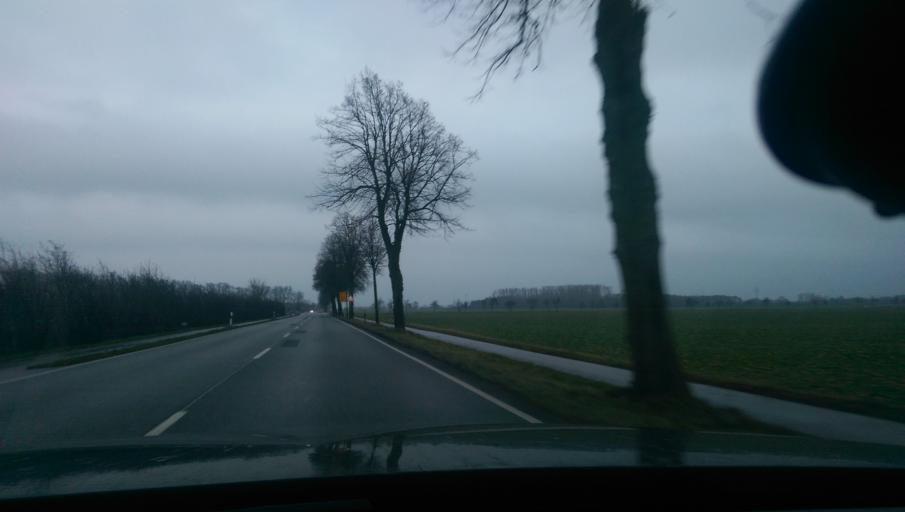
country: DE
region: Lower Saxony
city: Verden
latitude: 52.9101
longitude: 9.2171
